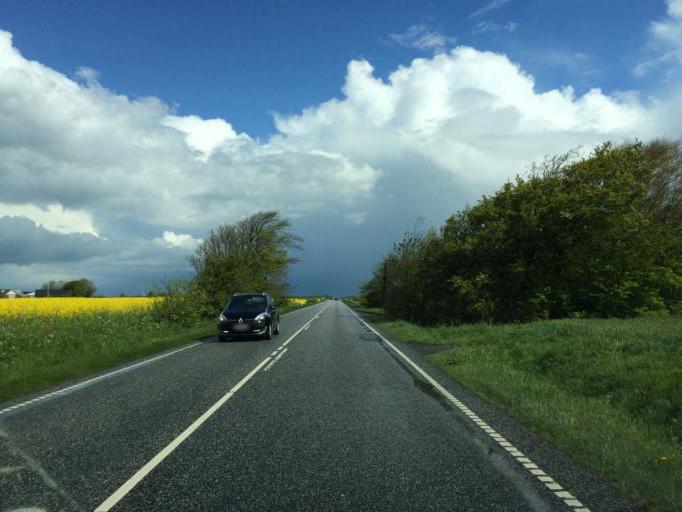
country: DK
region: Central Jutland
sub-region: Holstebro Kommune
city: Vinderup
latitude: 56.4283
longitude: 8.7111
